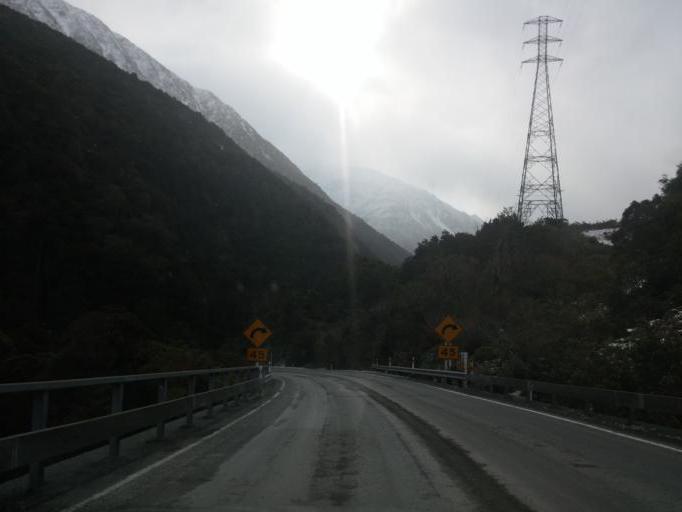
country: NZ
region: West Coast
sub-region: Grey District
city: Greymouth
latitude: -42.8835
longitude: 171.5559
